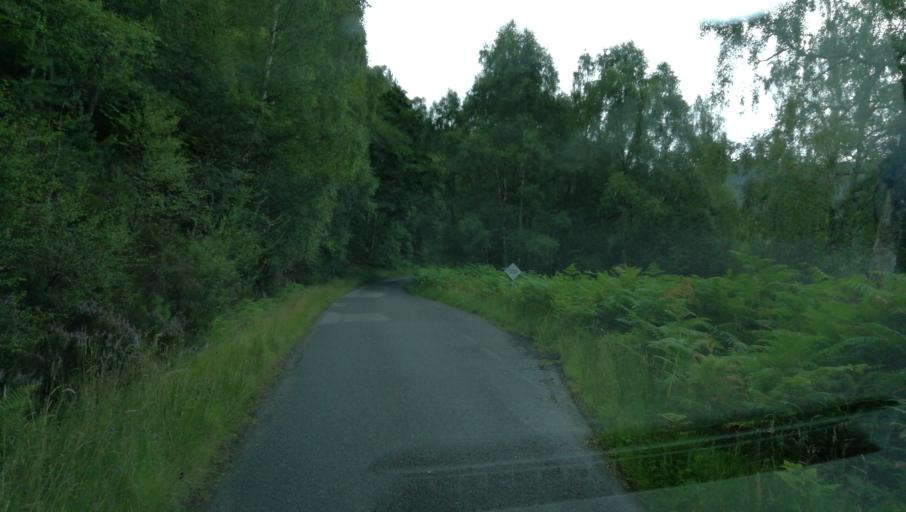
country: GB
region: Scotland
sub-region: Highland
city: Spean Bridge
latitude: 57.3015
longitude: -4.8935
